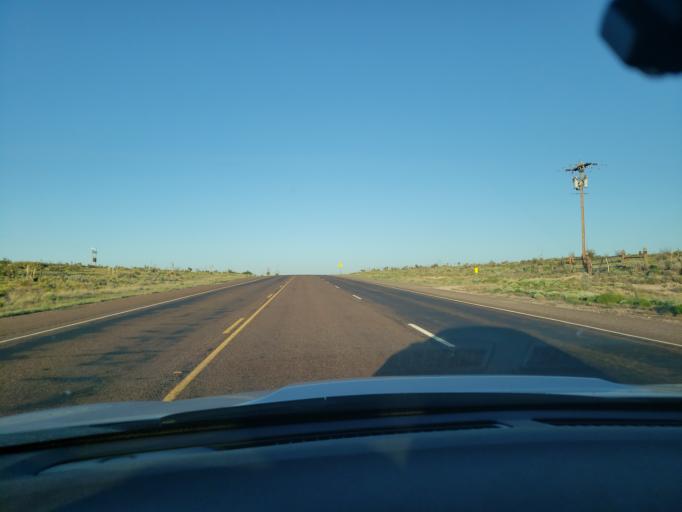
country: US
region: Texas
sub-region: El Paso County
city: Homestead Meadows South
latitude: 31.8272
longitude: -105.8875
